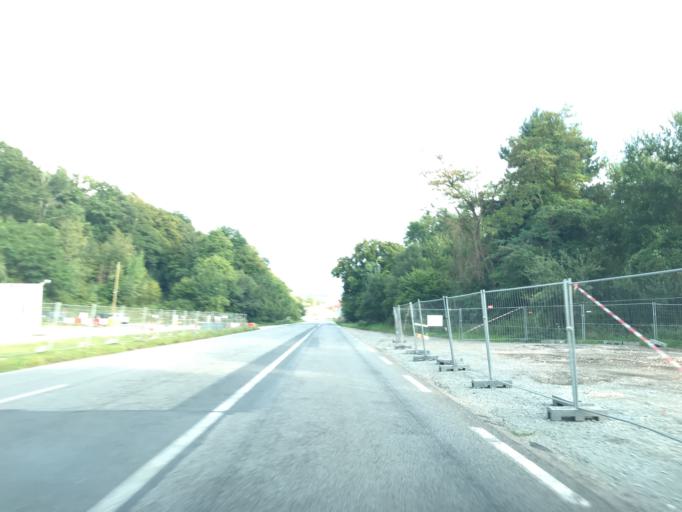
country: FR
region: Haute-Normandie
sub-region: Departement de la Seine-Maritime
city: Tancarville
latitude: 49.4810
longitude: 0.4534
